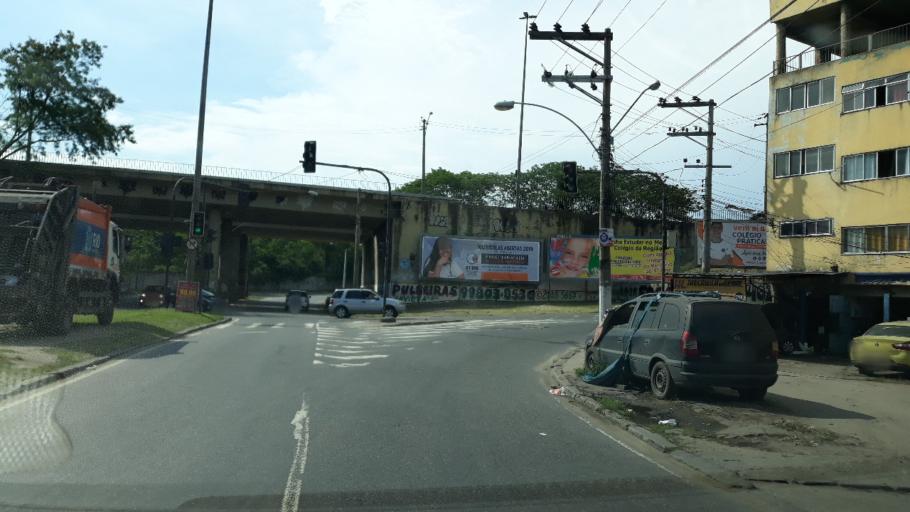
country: BR
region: Rio de Janeiro
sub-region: Sao Joao De Meriti
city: Sao Joao de Meriti
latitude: -22.8506
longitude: -43.3842
